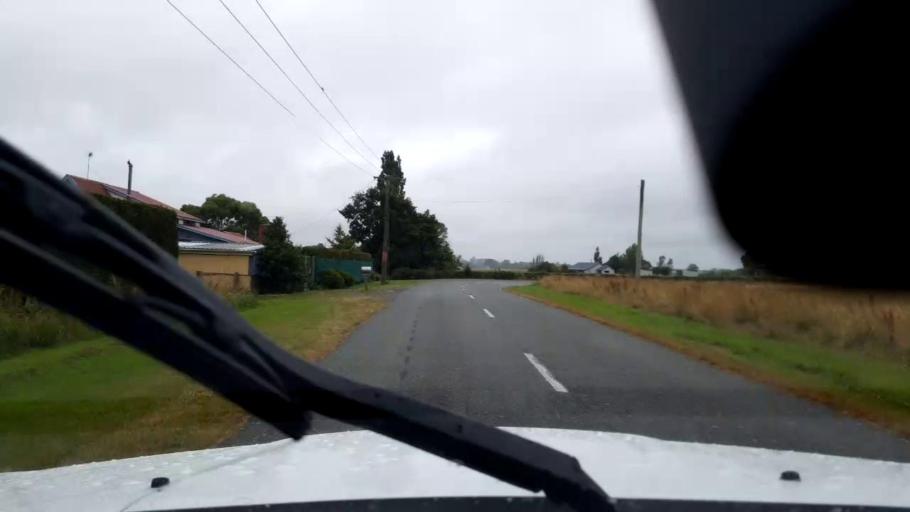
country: NZ
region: Canterbury
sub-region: Timaru District
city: Pleasant Point
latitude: -44.2511
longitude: 171.2343
